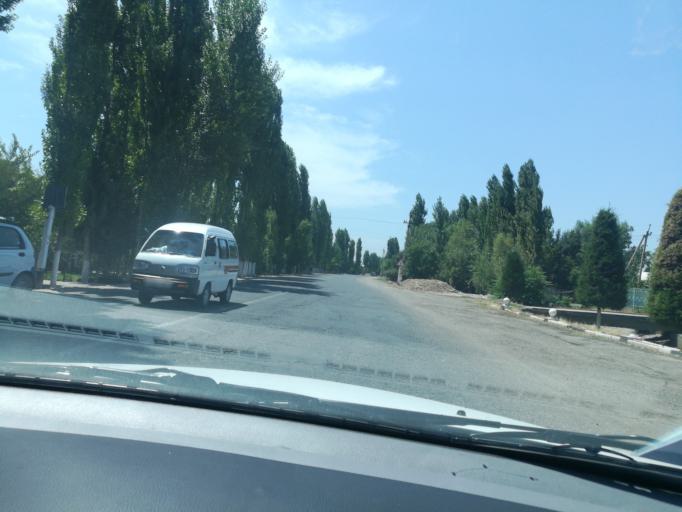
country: UZ
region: Namangan
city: Uchqurghon Shahri
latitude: 41.0765
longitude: 72.0523
